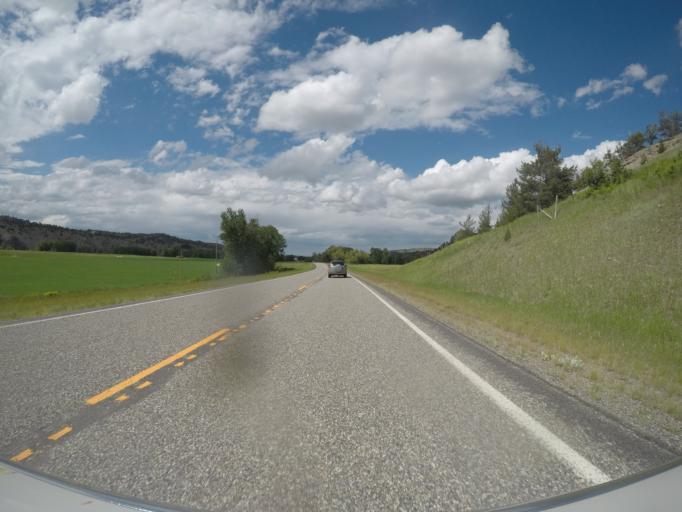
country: US
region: Montana
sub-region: Sweet Grass County
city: Big Timber
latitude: 45.7183
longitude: -109.9977
